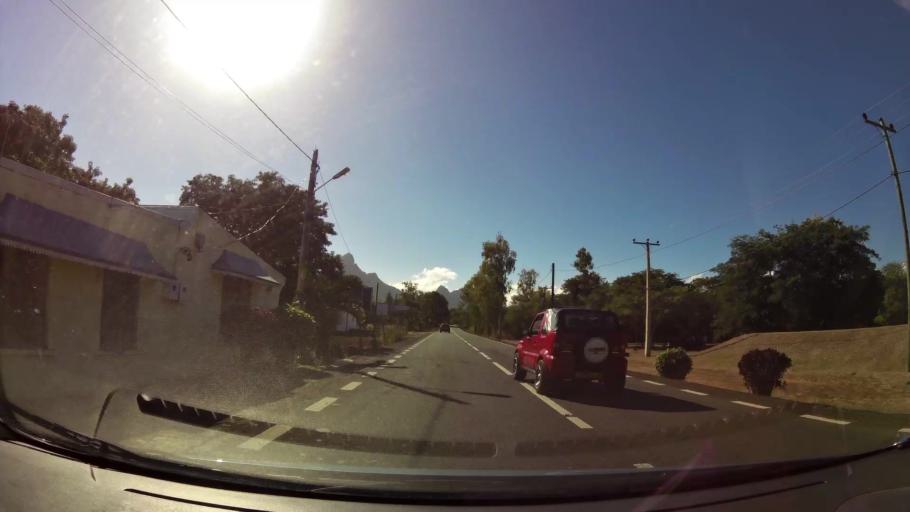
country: MU
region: Black River
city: Tamarin
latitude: -20.3273
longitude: 57.3865
